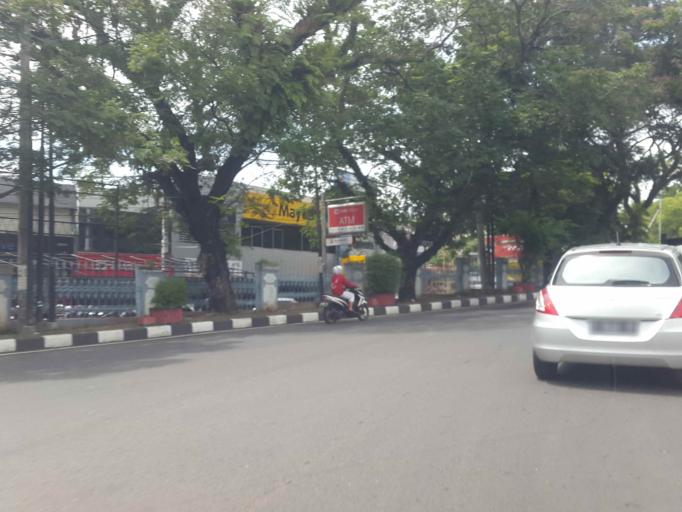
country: ID
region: Central Java
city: Semarang
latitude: -7.0081
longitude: 110.4162
